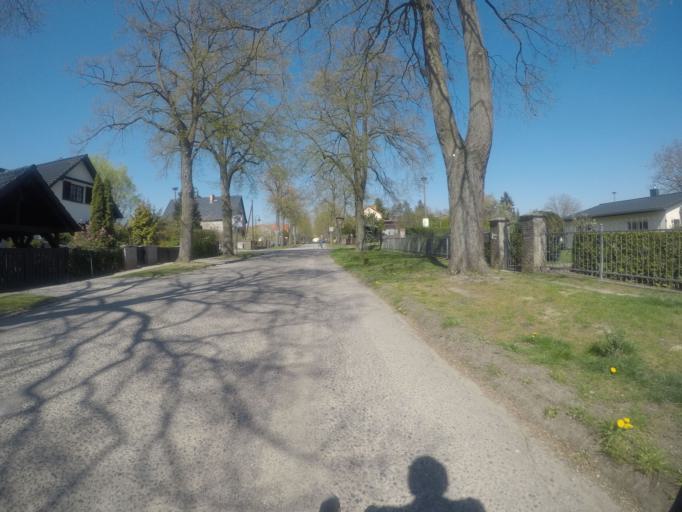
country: DE
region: Brandenburg
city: Bernau bei Berlin
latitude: 52.6851
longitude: 13.5894
